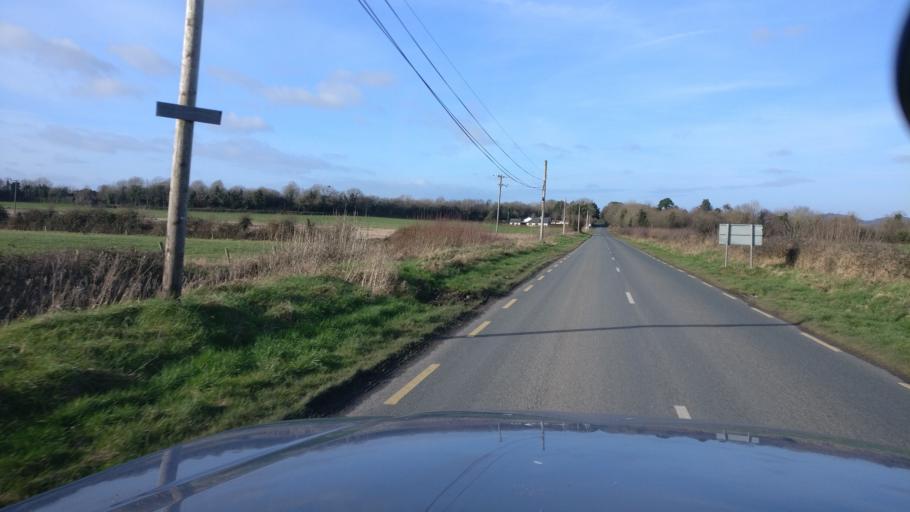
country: IE
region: Leinster
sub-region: Laois
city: Stradbally
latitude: 52.9632
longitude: -7.2034
